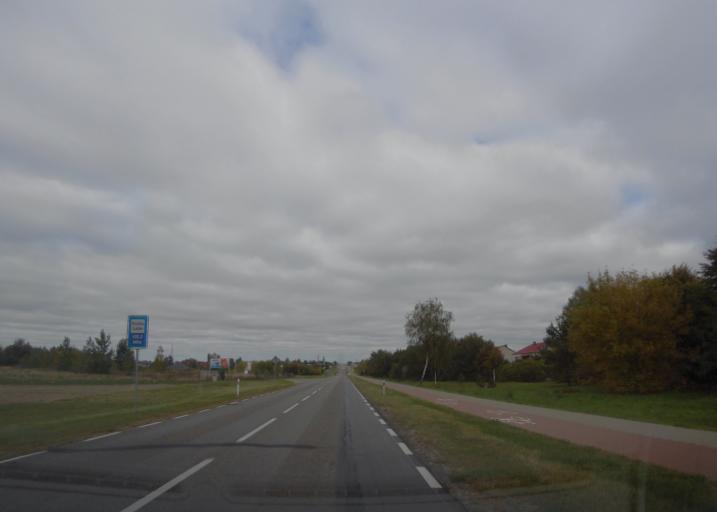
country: PL
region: Lublin Voivodeship
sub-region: Powiat wlodawski
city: Wlodawa
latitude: 51.5350
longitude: 23.5315
